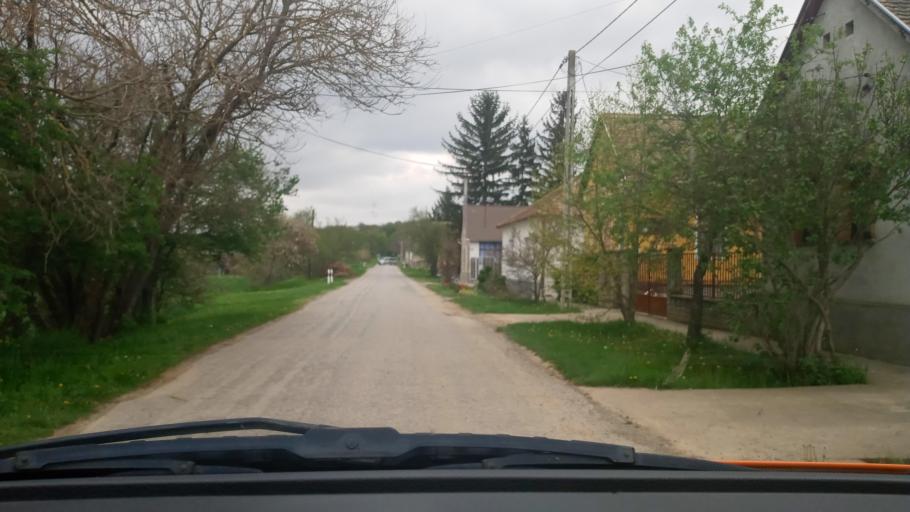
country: HU
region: Baranya
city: Boly
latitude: 46.0092
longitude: 18.5474
